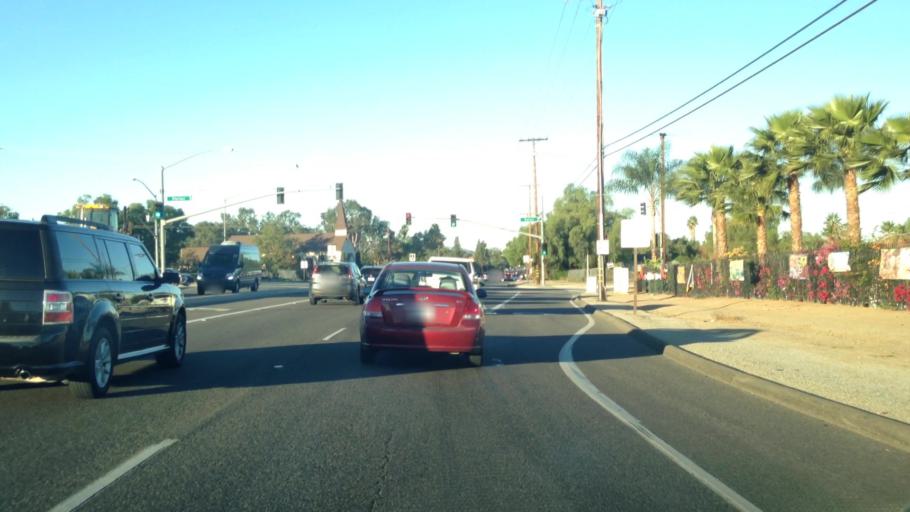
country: US
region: California
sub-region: Riverside County
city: Woodcrest
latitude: 33.8825
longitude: -117.3566
